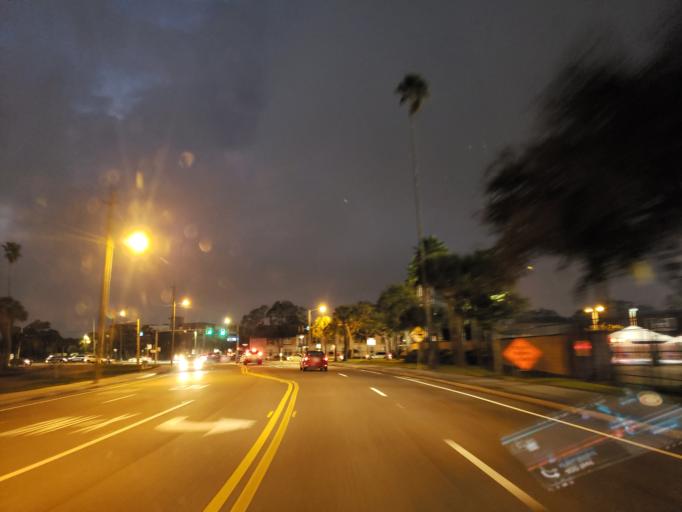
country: US
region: Florida
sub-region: Hillsborough County
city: Tampa
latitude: 27.9503
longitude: -82.4673
